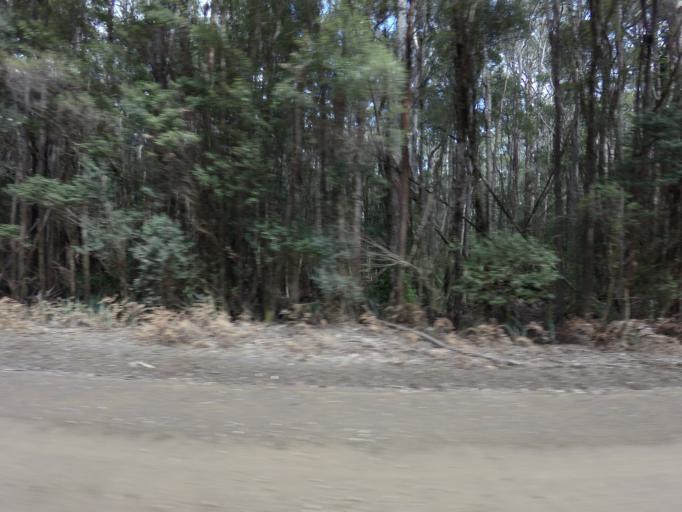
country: AU
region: Tasmania
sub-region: Huon Valley
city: Geeveston
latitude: -43.3963
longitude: 146.8594
